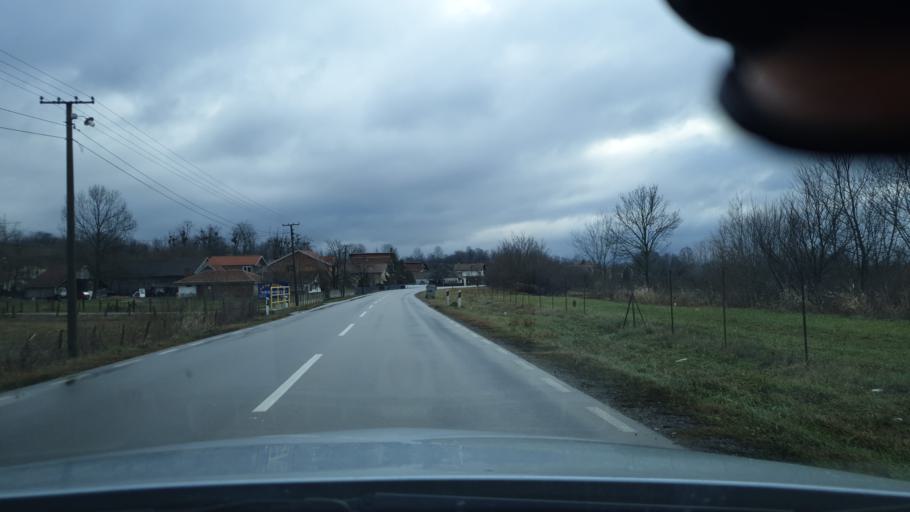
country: RS
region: Central Serbia
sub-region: Branicevski Okrug
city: Petrovac
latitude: 44.4399
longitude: 21.3456
